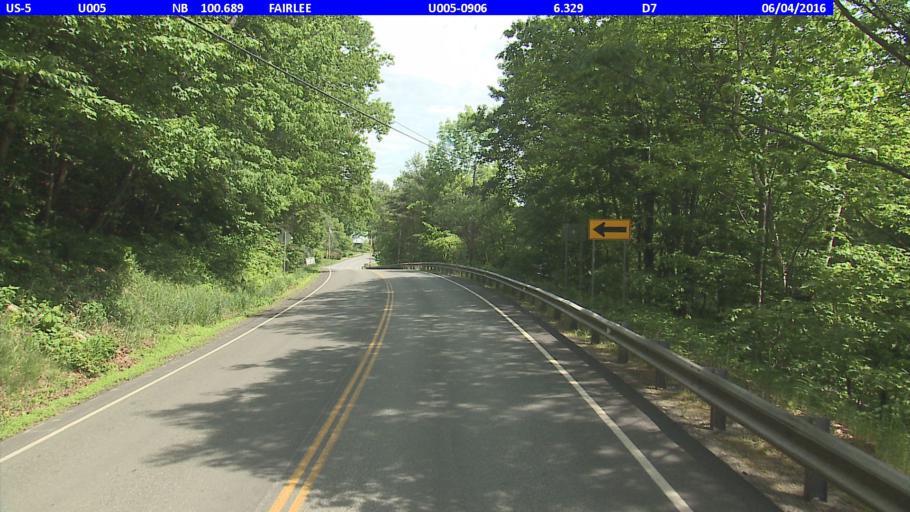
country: US
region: New Hampshire
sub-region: Grafton County
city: Orford
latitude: 43.9479
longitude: -72.1181
